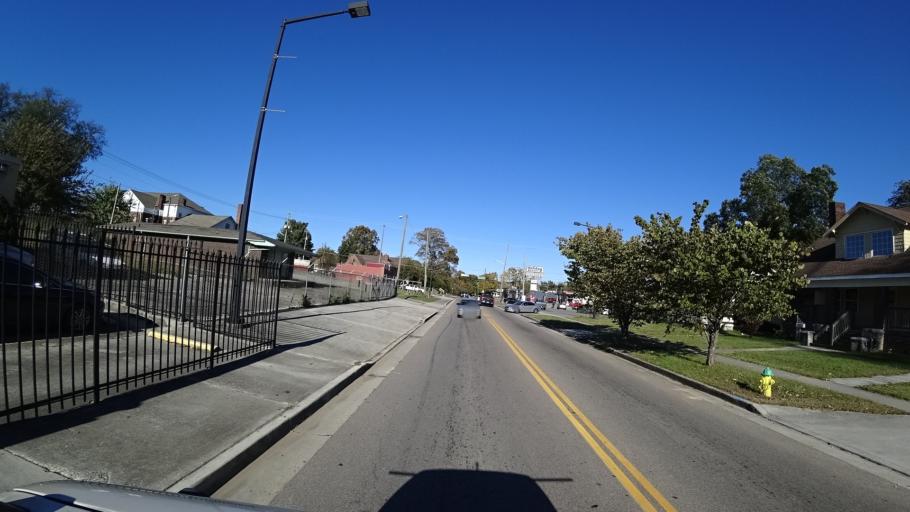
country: US
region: Tennessee
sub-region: Knox County
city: Knoxville
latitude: 35.9824
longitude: -83.8943
